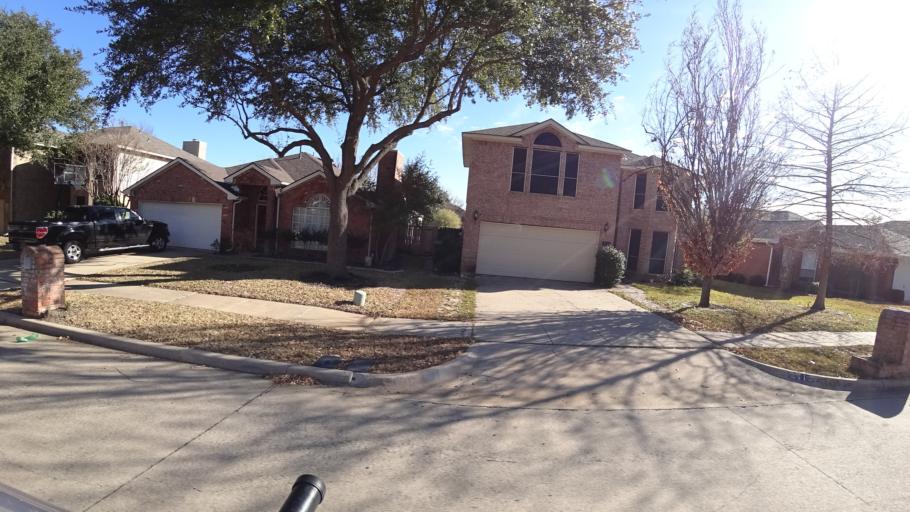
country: US
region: Texas
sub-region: Denton County
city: Lewisville
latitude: 33.0149
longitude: -97.0347
